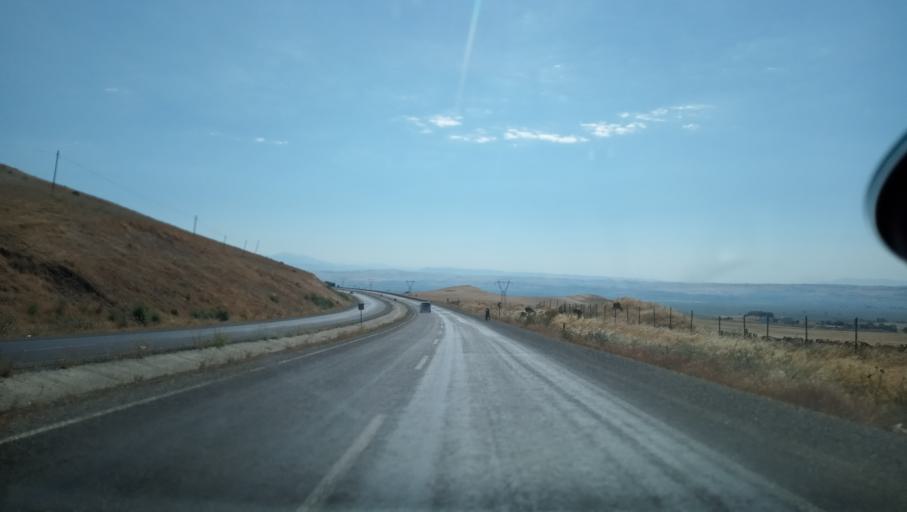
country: TR
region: Diyarbakir
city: Malabadi
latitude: 38.1180
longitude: 41.1390
